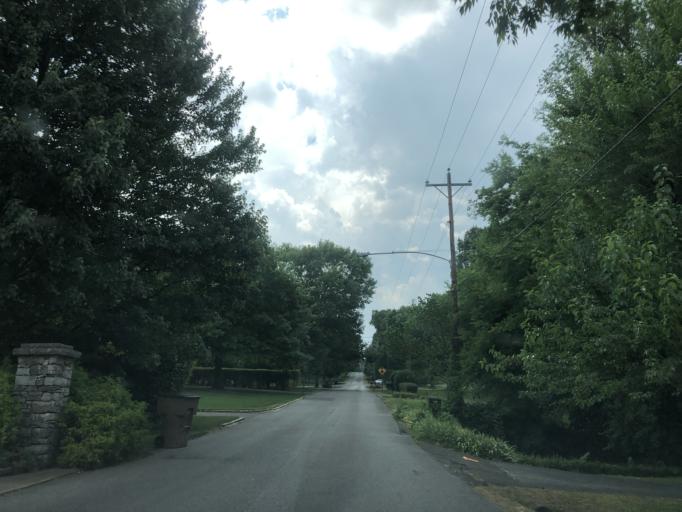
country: US
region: Tennessee
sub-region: Davidson County
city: Oak Hill
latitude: 36.1164
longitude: -86.8138
